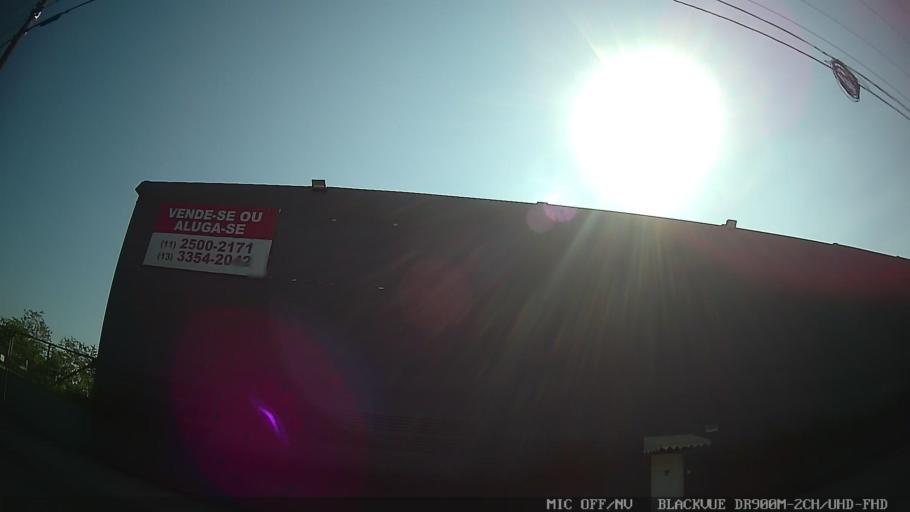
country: BR
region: Sao Paulo
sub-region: Guaruja
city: Guaruja
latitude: -24.0066
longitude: -46.2934
